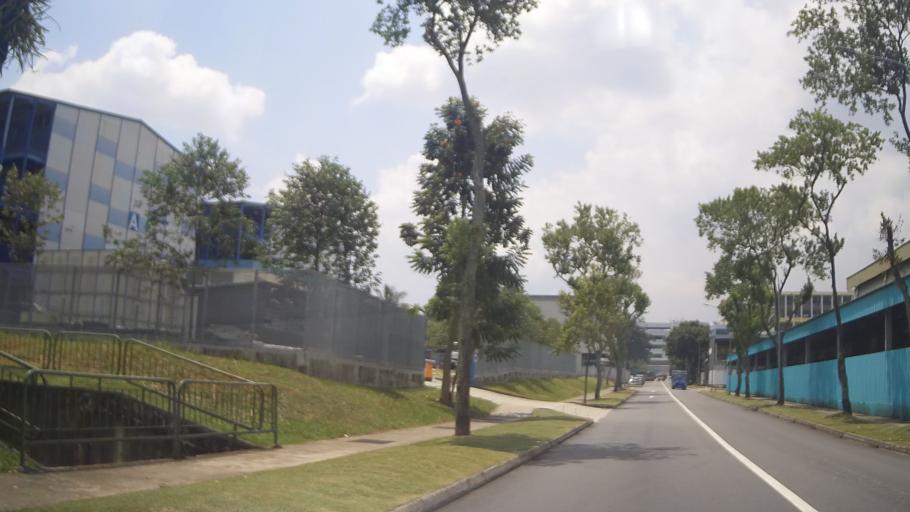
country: MY
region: Johor
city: Johor Bahru
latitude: 1.4509
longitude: 103.7987
